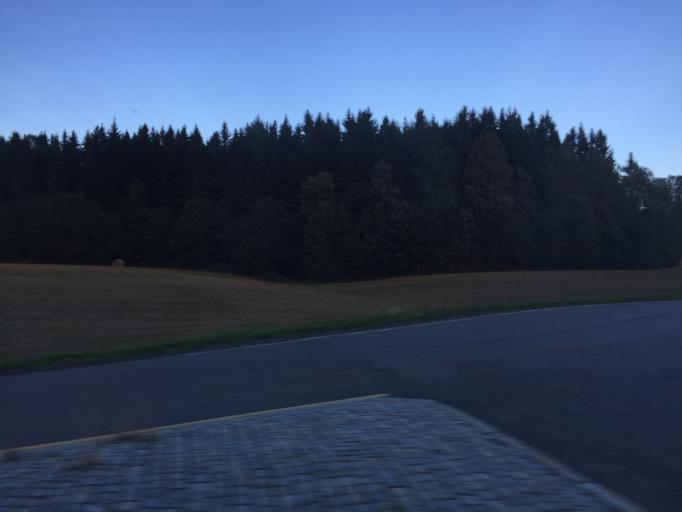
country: NO
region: Akershus
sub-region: Lorenskog
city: Kjenn
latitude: 59.9347
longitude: 11.0008
